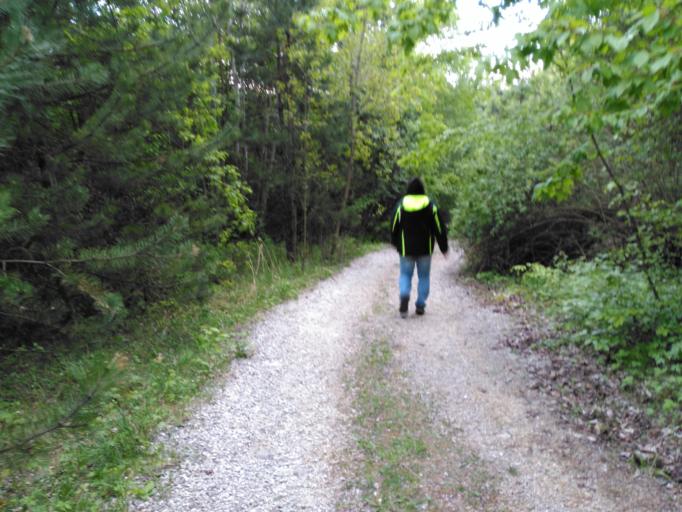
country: CZ
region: Central Bohemia
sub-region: Okres Beroun
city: Kraluv Dvur
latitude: 49.9189
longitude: 14.0581
